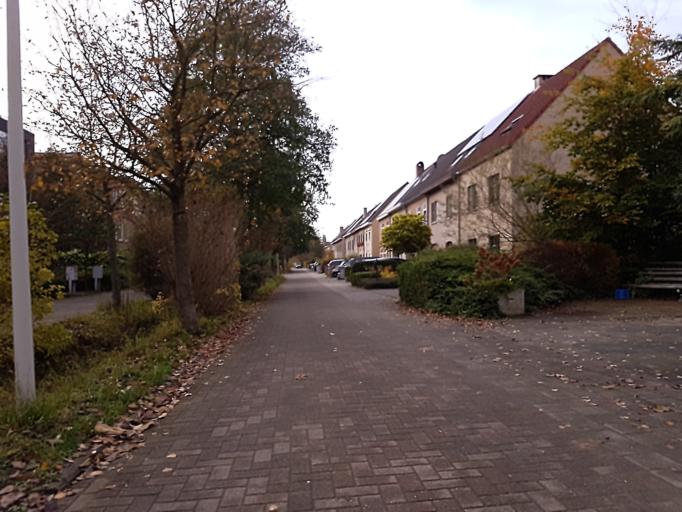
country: BE
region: Flanders
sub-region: Provincie Antwerpen
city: Wommelgem
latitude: 51.1779
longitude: 4.5289
